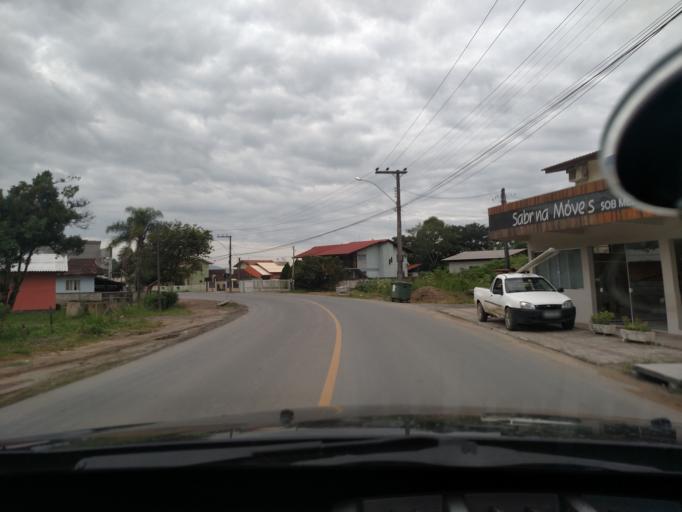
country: BR
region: Santa Catarina
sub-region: Porto Belo
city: Porto Belo
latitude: -27.1629
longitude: -48.5194
